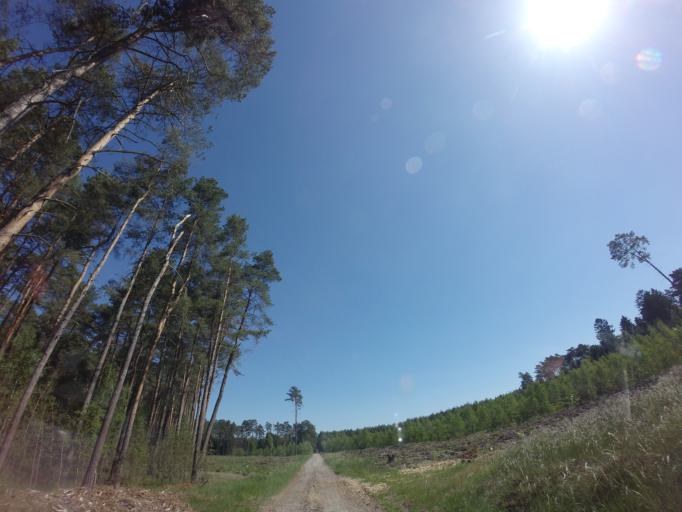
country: PL
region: West Pomeranian Voivodeship
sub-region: Powiat drawski
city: Kalisz Pomorski
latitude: 53.1549
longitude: 15.9753
